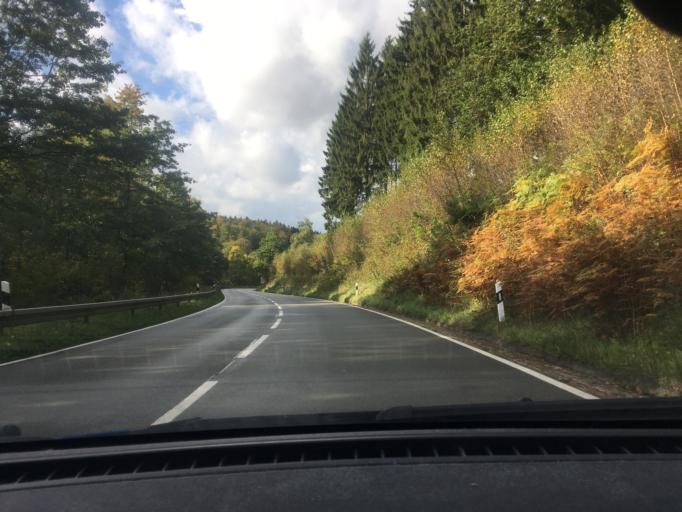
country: DE
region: Lower Saxony
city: Bevern
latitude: 51.8011
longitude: 9.4997
